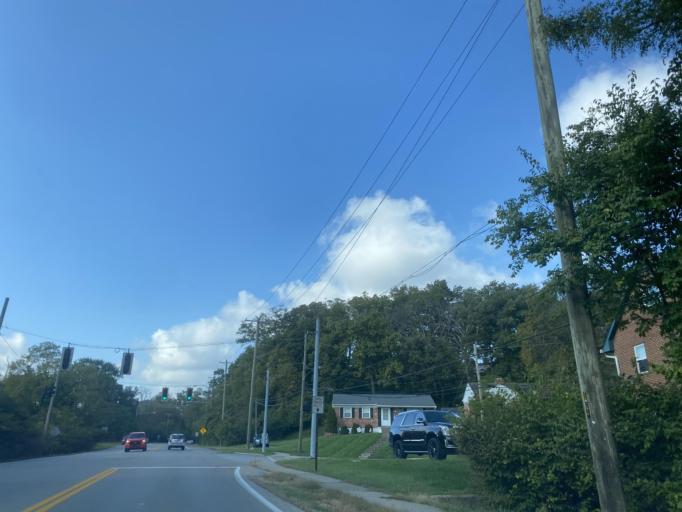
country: US
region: Kentucky
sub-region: Campbell County
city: Fort Thomas
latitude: 39.0910
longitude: -84.4564
